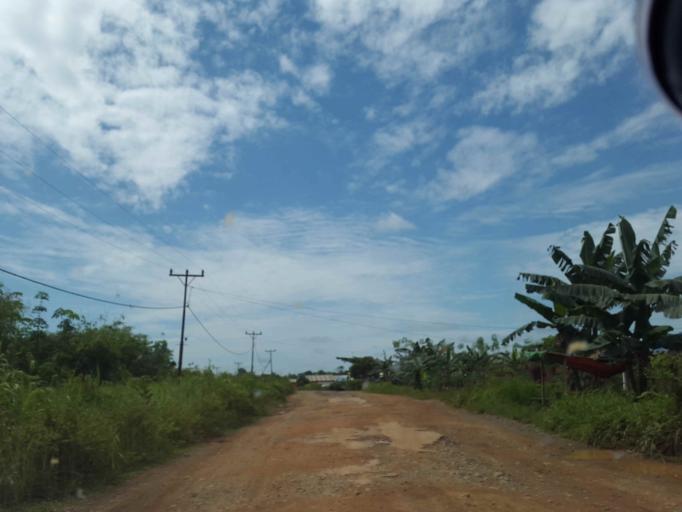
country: MY
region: Sarawak
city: Kuching
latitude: 0.8186
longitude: 110.5458
